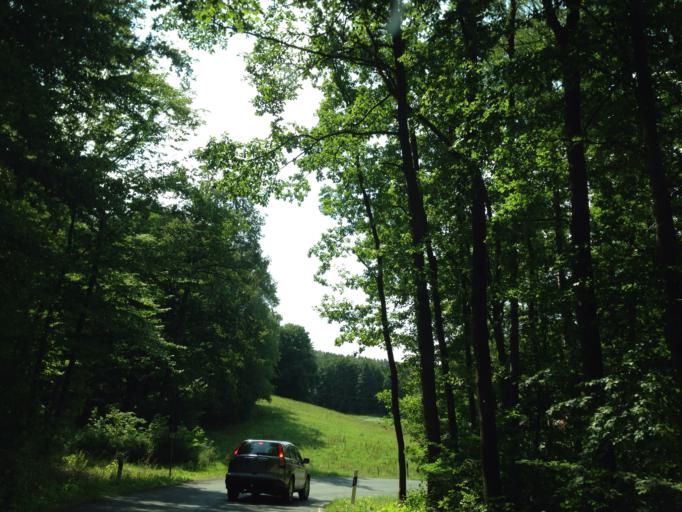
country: DE
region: Thuringia
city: Herschdorf
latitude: 50.7297
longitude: 11.5181
